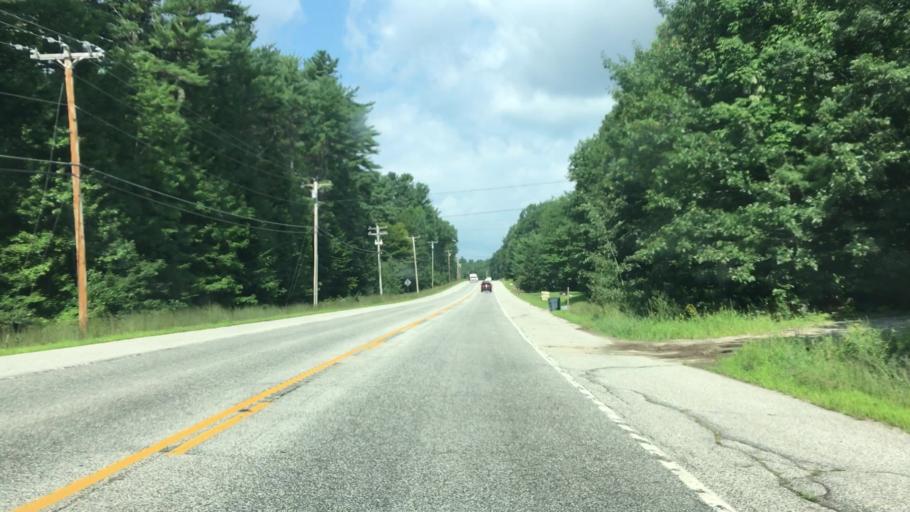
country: US
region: Maine
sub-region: Cumberland County
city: Raymond
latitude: 43.9032
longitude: -70.4818
